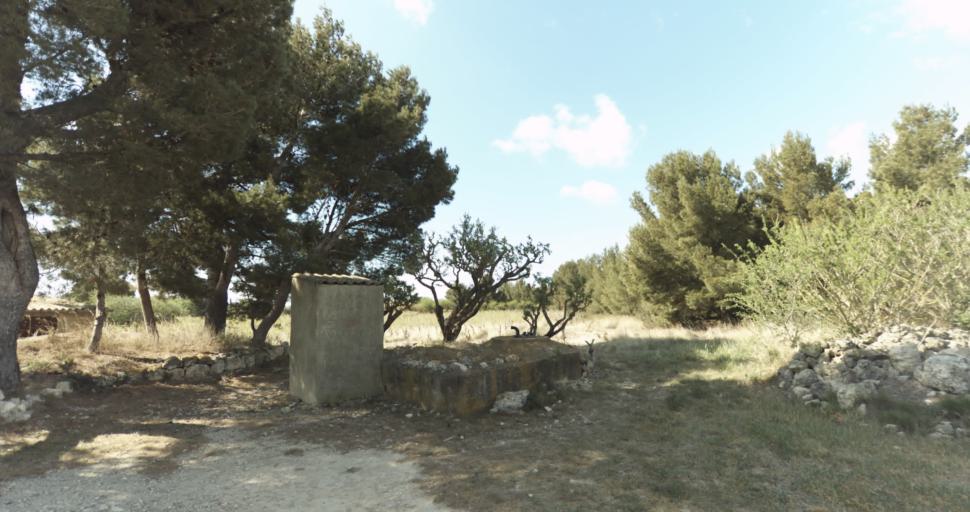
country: FR
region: Languedoc-Roussillon
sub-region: Departement de l'Aude
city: Leucate
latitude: 42.9299
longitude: 3.0370
